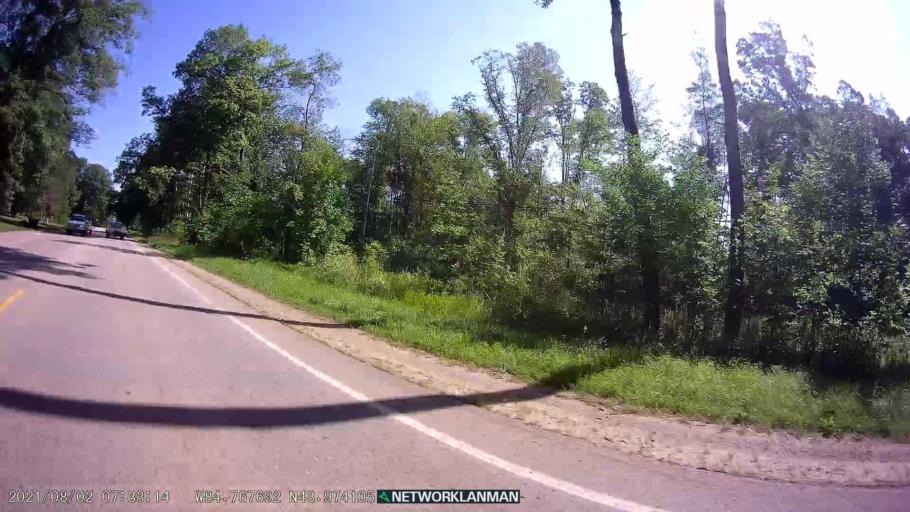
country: US
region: Michigan
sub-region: Clare County
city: Harrison
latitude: 43.9744
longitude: -84.7678
